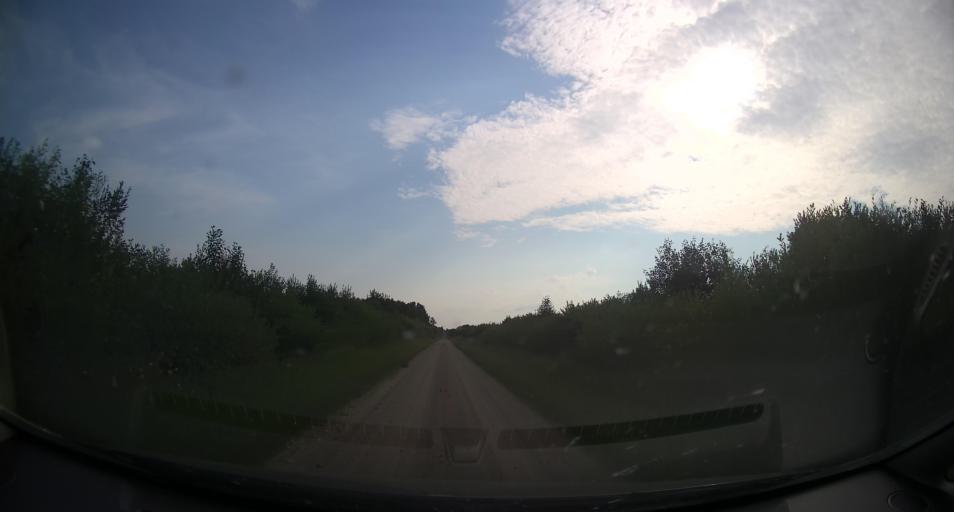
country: EE
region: Laeaene
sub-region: Lihula vald
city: Lihula
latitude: 58.6673
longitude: 23.8181
